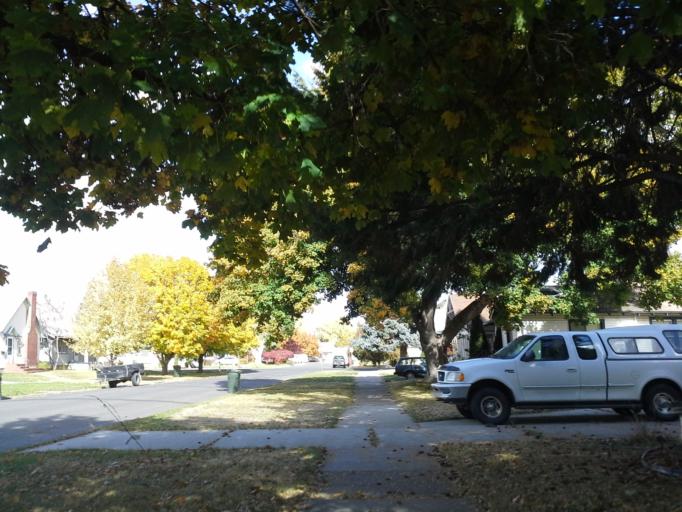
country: US
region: Oregon
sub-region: Baker County
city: Baker City
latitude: 44.7845
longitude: -117.8318
